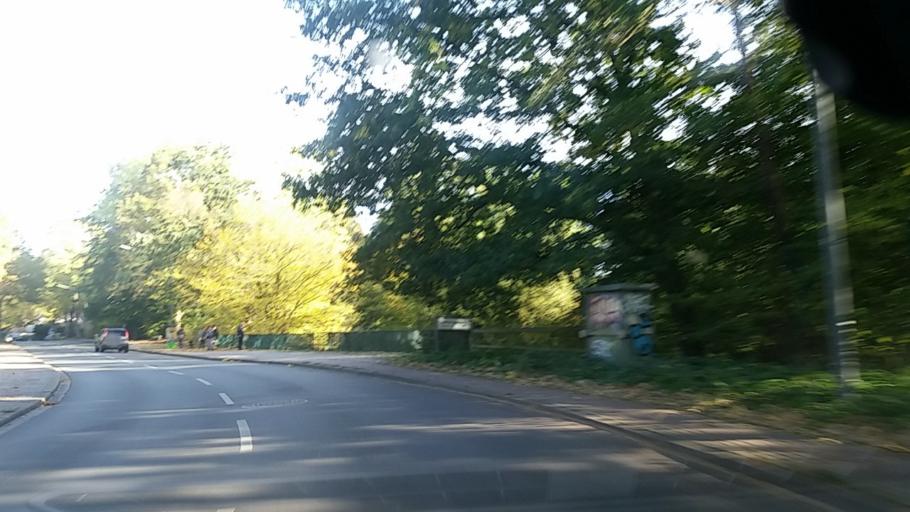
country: DE
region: Hamburg
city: Duvenstedt
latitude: 53.7049
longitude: 10.1175
